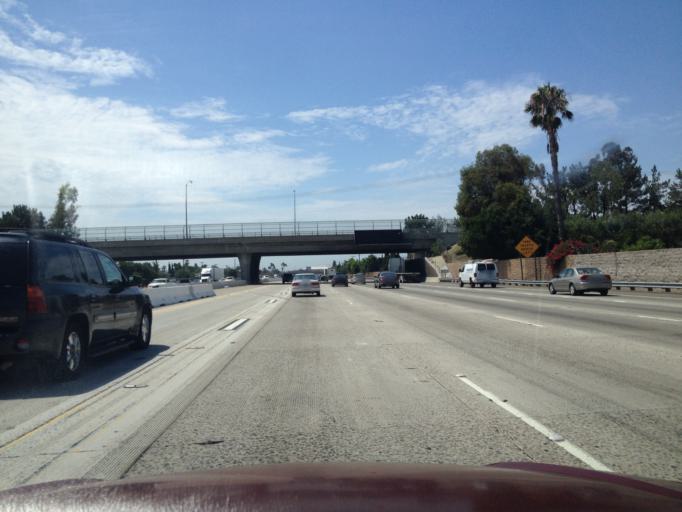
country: US
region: California
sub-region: Orange County
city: Anaheim
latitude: 33.8266
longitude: -117.8762
